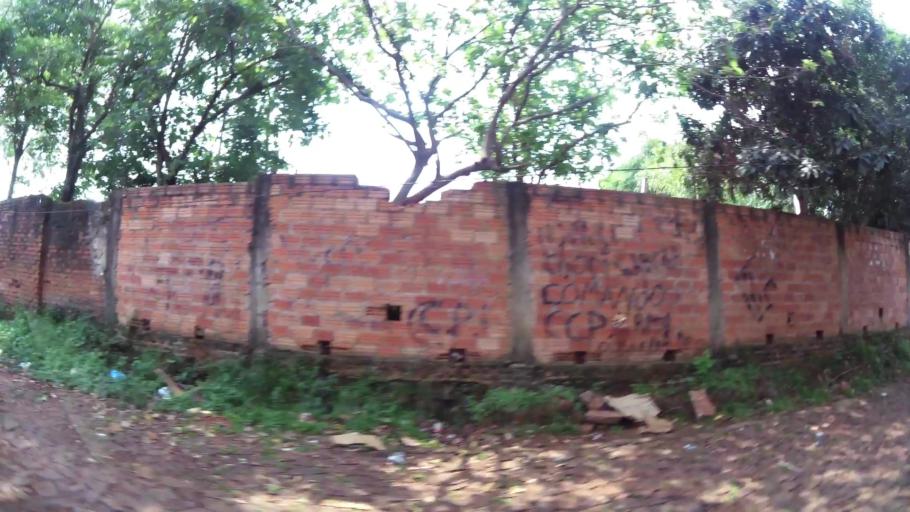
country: BR
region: Parana
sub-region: Foz Do Iguacu
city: Foz do Iguacu
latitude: -25.5645
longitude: -54.6017
